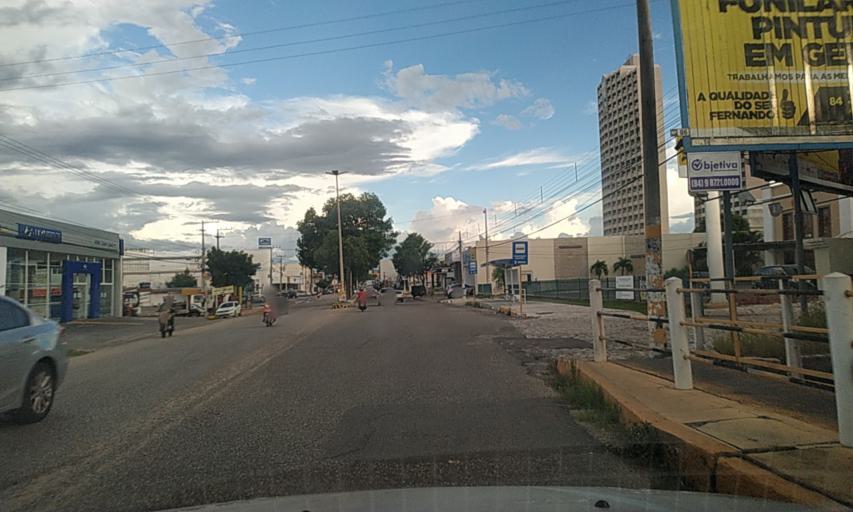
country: BR
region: Rio Grande do Norte
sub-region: Mossoro
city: Mossoro
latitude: -5.2001
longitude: -37.3394
